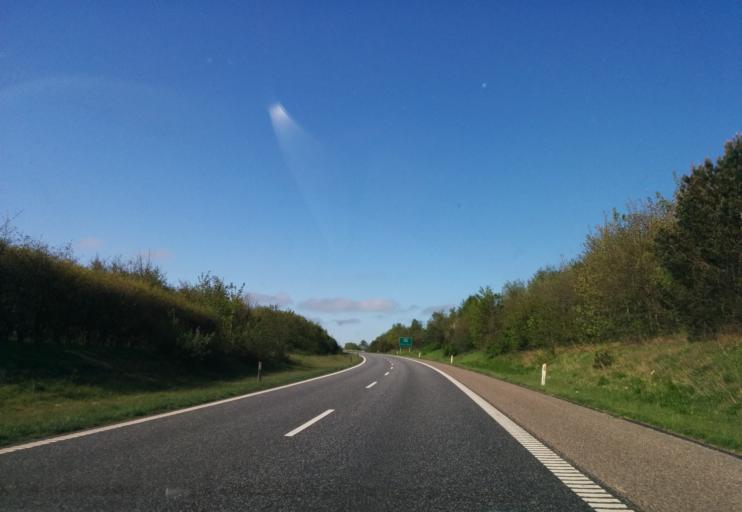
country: DK
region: Central Jutland
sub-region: Skanderborg Kommune
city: Horning
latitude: 56.1017
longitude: 10.0346
